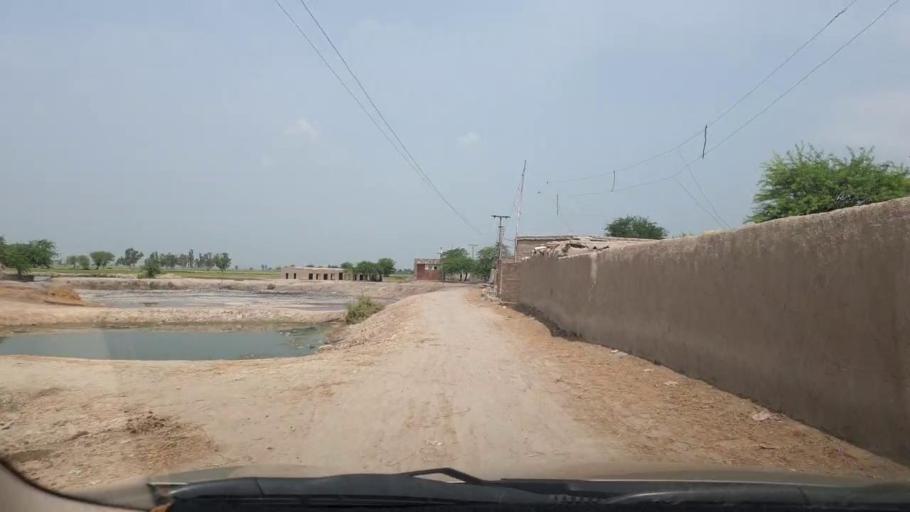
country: PK
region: Sindh
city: Goth Garelo
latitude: 27.5096
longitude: 68.1322
